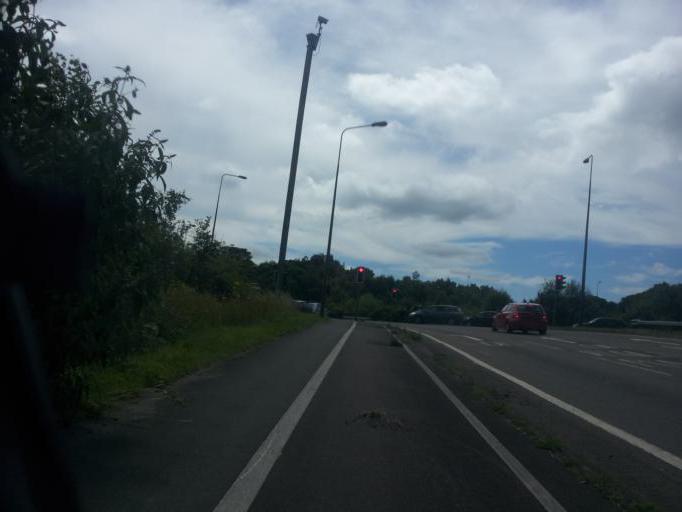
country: GB
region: England
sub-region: Kent
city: Aylesford
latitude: 51.3373
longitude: 0.5051
